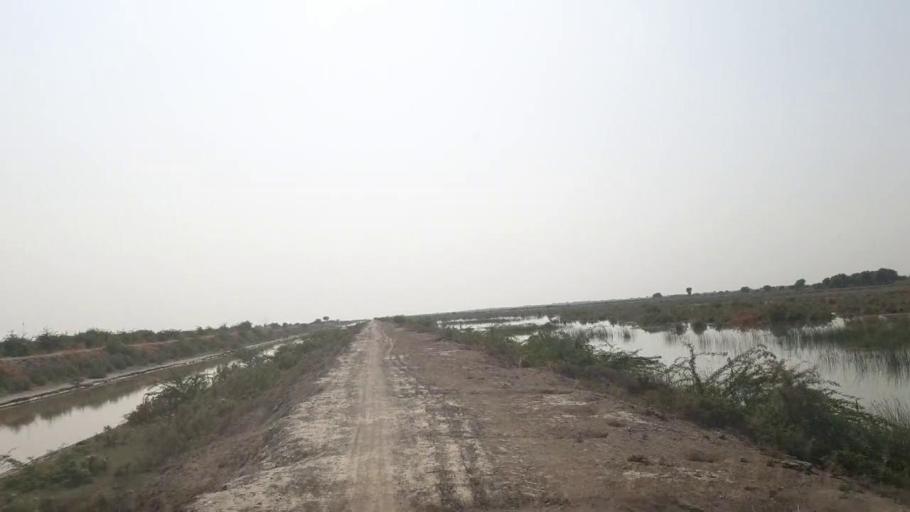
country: PK
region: Sindh
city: Kadhan
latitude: 24.3900
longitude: 68.9019
